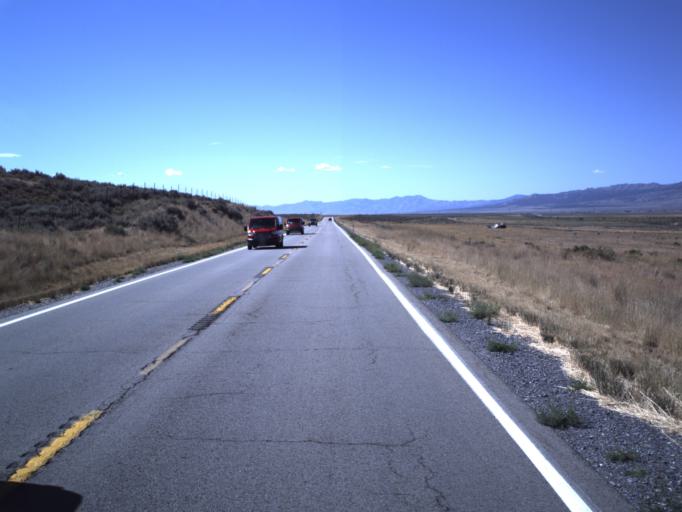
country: US
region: Utah
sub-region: Tooele County
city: Tooele
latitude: 40.4202
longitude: -112.3820
